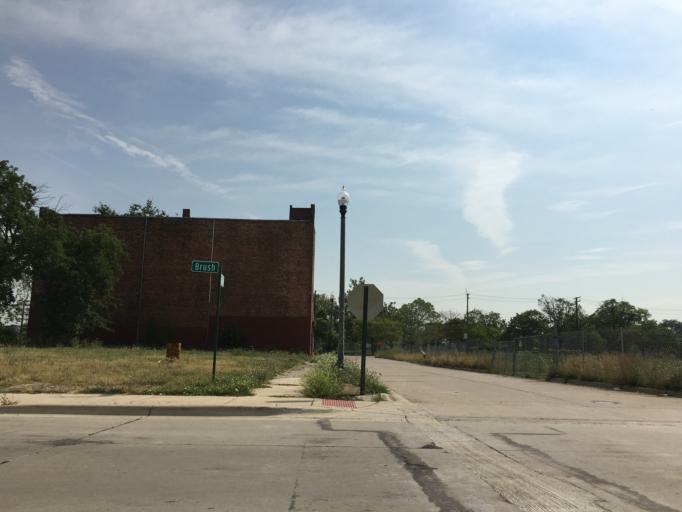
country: US
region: Michigan
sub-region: Wayne County
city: Detroit
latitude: 42.3441
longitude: -83.0502
